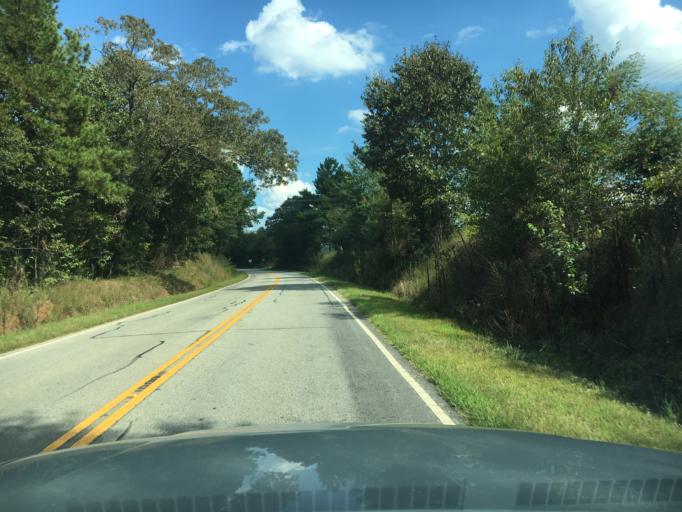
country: US
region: South Carolina
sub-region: Oconee County
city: Utica
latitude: 34.7124
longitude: -82.9021
